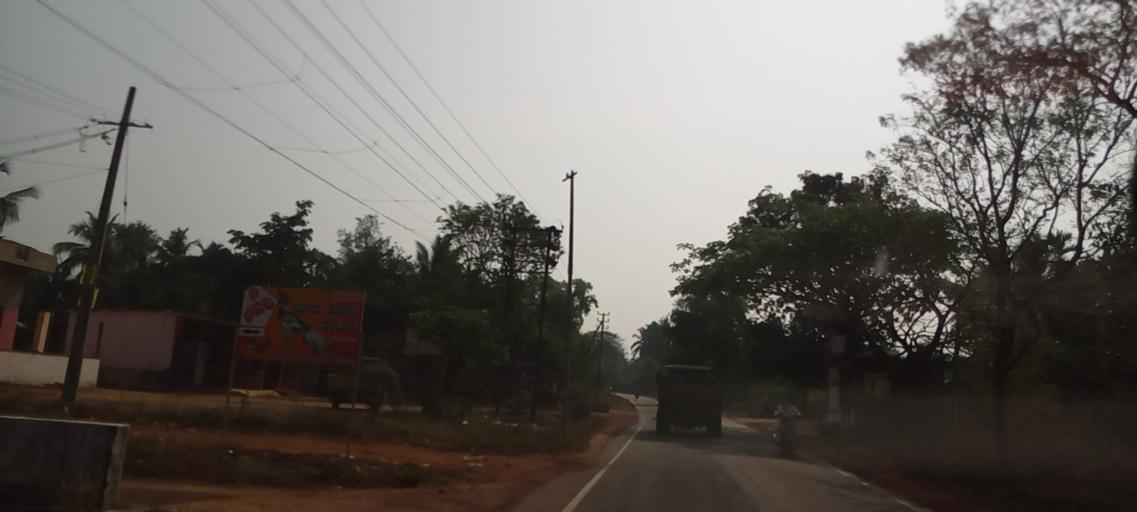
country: IN
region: Karnataka
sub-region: Udupi
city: Coondapoor
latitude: 13.5156
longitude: 74.7510
